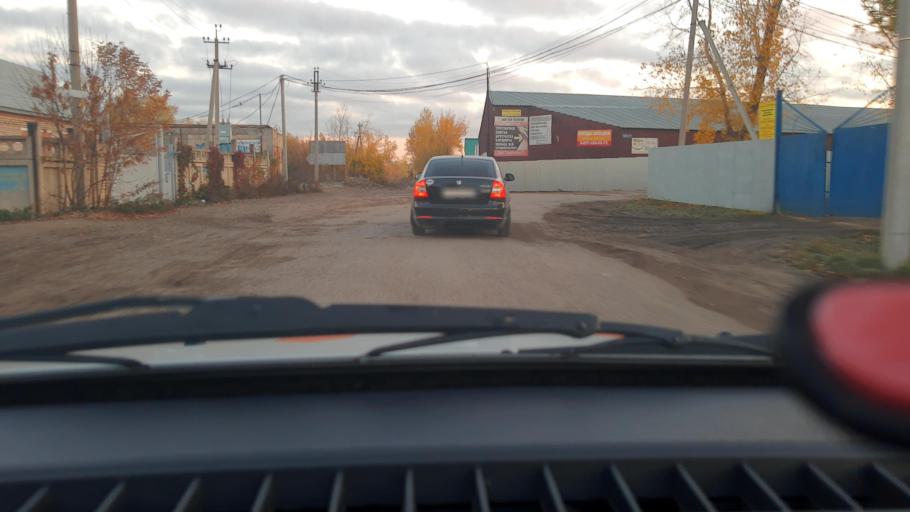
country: RU
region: Bashkortostan
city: Mikhaylovka
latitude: 54.7512
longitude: 55.9068
